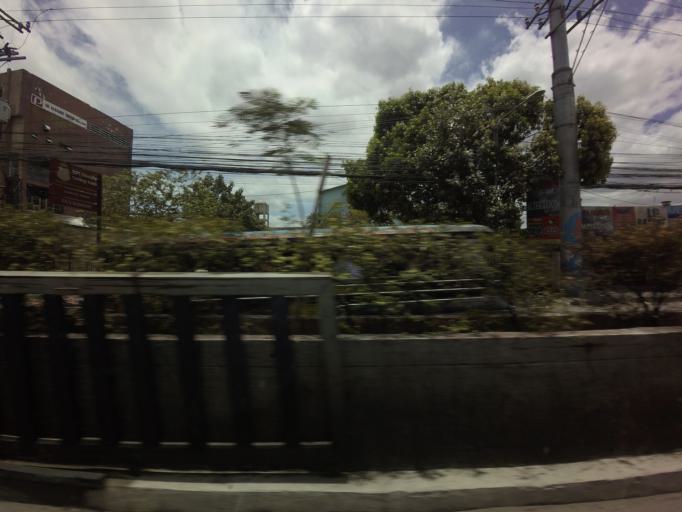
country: PH
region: Metro Manila
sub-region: Marikina
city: Calumpang
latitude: 14.6179
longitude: 121.1016
